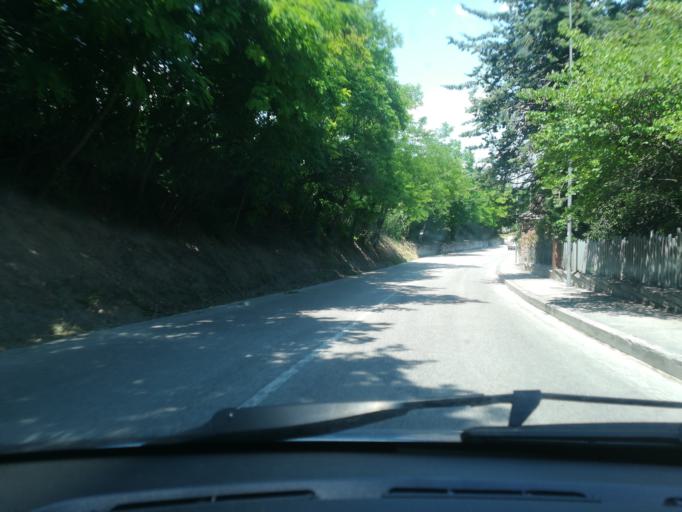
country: IT
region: The Marches
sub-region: Provincia di Macerata
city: Villa Potenza
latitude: 43.3098
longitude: 13.4363
